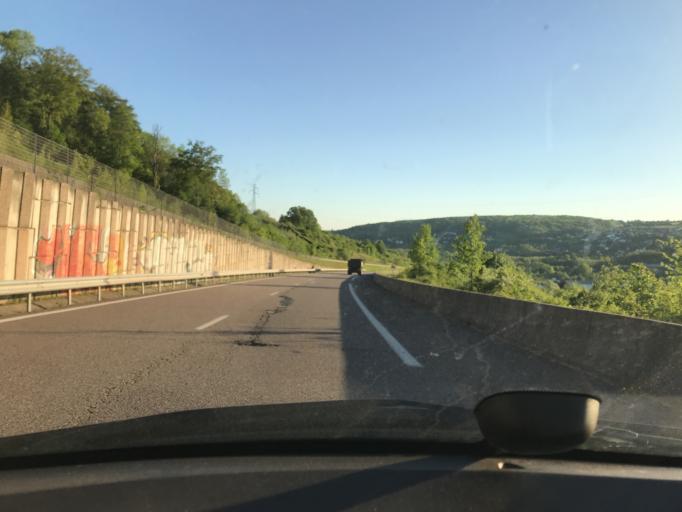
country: DE
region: Saarland
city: Kleinblittersdorf
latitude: 49.1348
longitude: 7.0388
